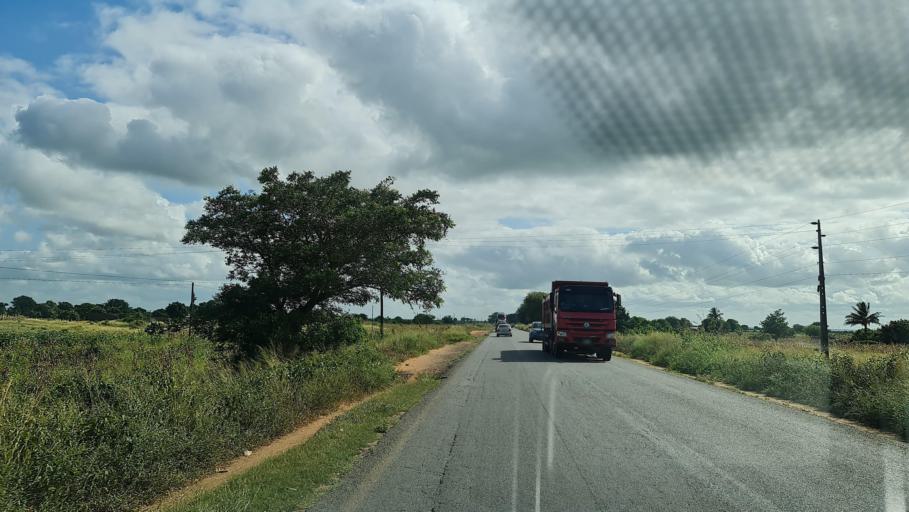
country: MZ
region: Gaza
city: Macia
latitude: -25.0854
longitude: 32.8456
